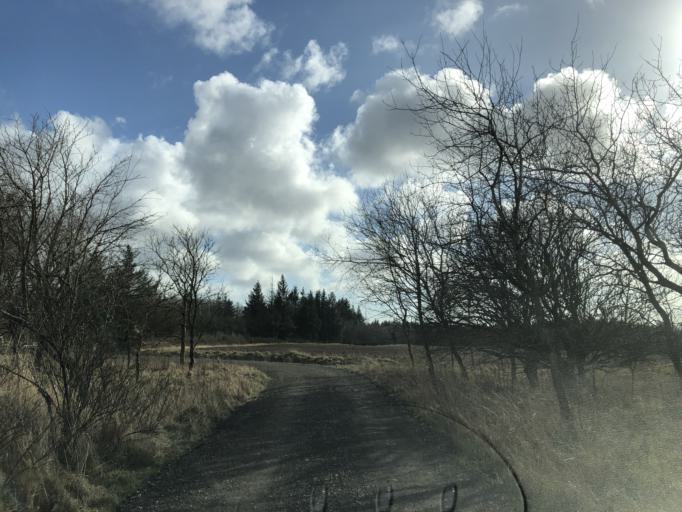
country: DK
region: Central Jutland
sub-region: Holstebro Kommune
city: Ulfborg
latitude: 56.2781
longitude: 8.3470
